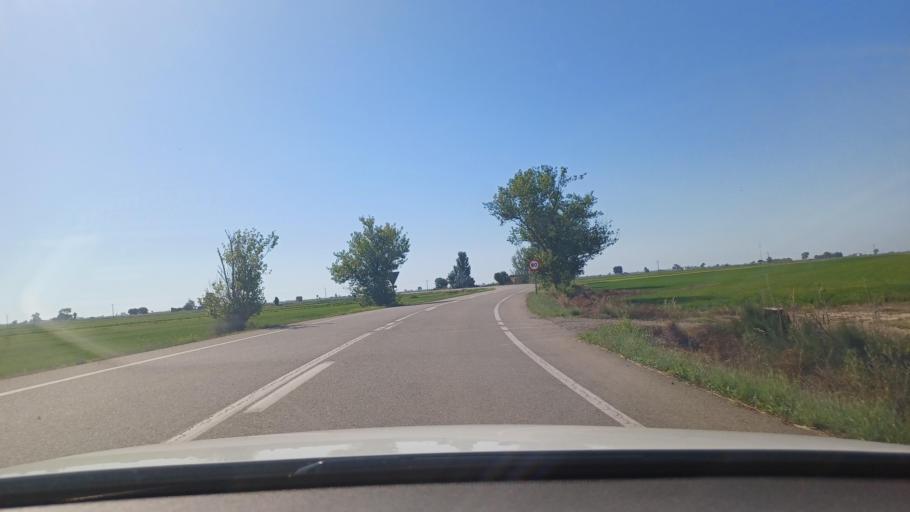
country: ES
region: Catalonia
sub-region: Provincia de Tarragona
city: Amposta
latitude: 40.7066
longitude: 0.6408
